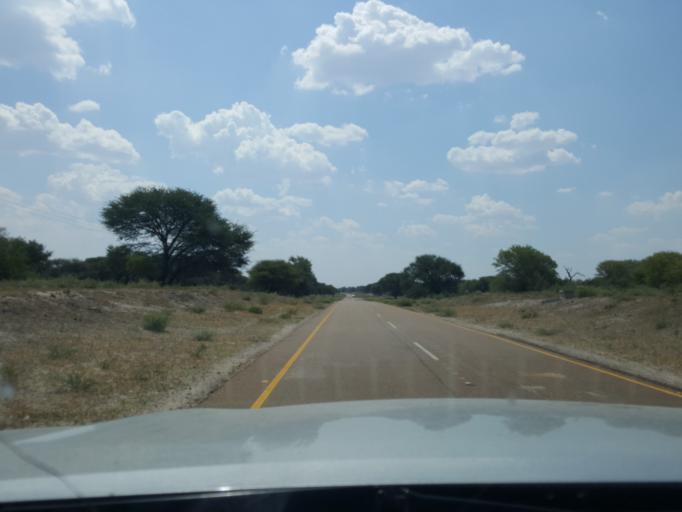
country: BW
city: Nokaneng
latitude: -19.8153
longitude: 22.2202
